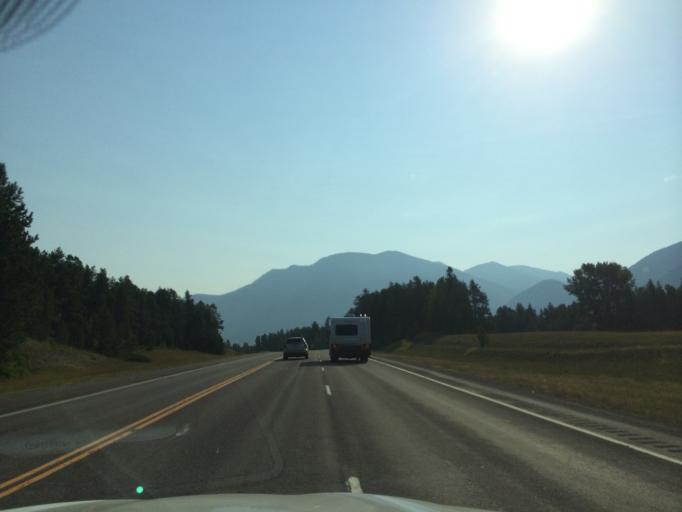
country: US
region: Montana
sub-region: Flathead County
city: Columbia Falls
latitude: 48.4511
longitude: -114.0226
